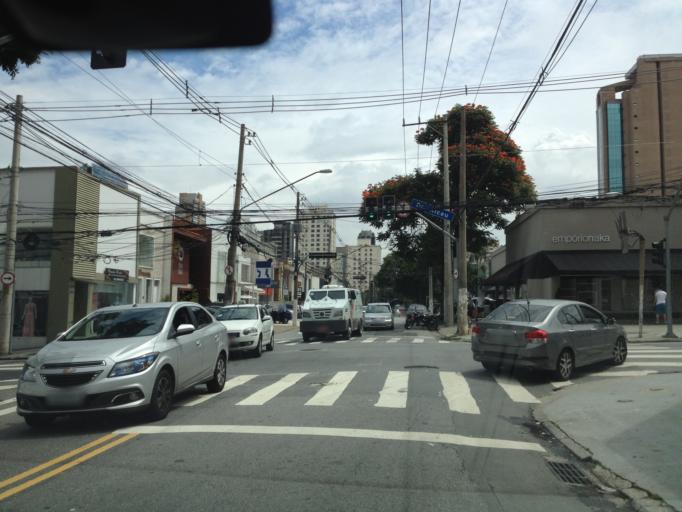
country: BR
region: Sao Paulo
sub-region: Sao Paulo
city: Sao Paulo
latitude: -23.5912
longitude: -46.6757
